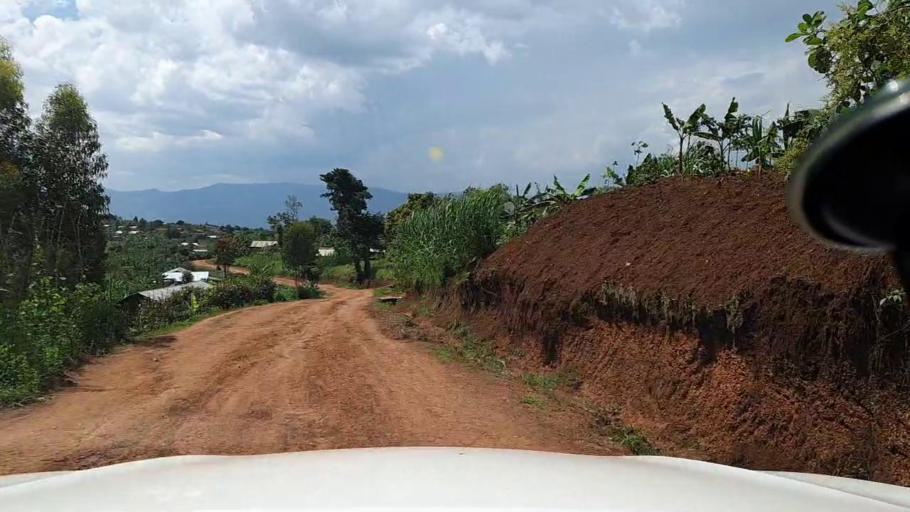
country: RW
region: Kigali
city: Kigali
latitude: -1.8331
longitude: 29.8415
